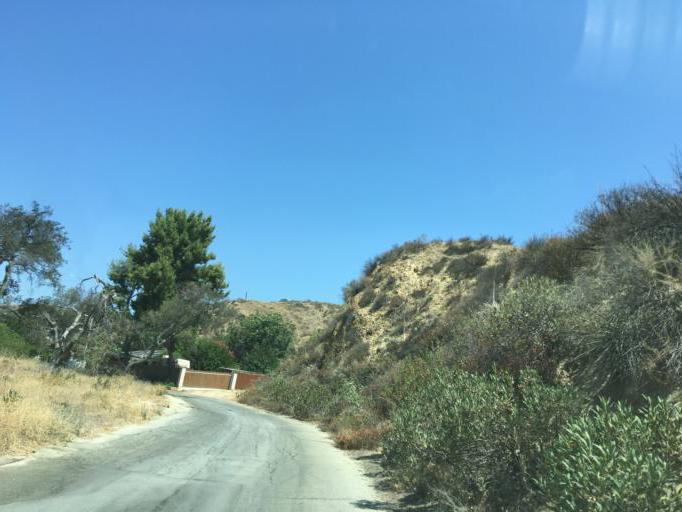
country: US
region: California
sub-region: Los Angeles County
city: Val Verde
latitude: 34.4433
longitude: -118.6558
